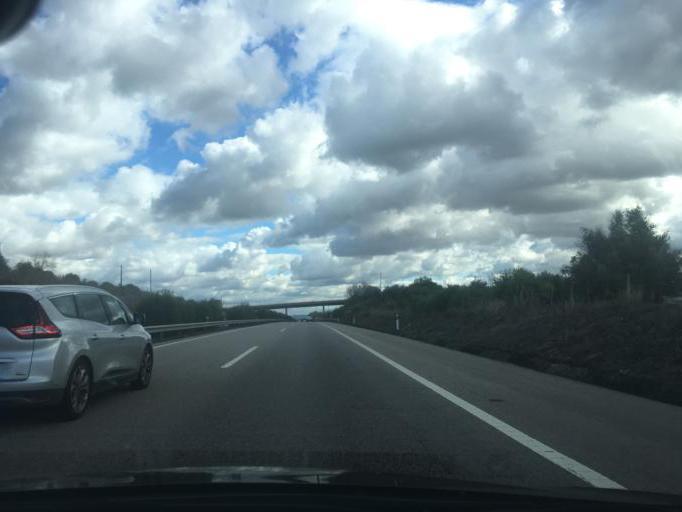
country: PT
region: Santarem
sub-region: Torres Novas
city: Torres Novas
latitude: 39.4687
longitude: -8.5669
